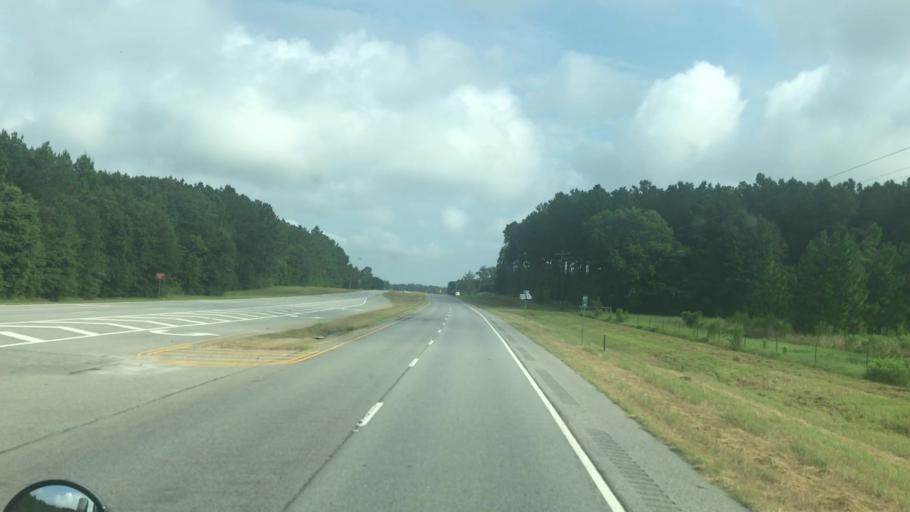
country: US
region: Georgia
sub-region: Miller County
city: Colquitt
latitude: 31.2275
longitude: -84.7812
